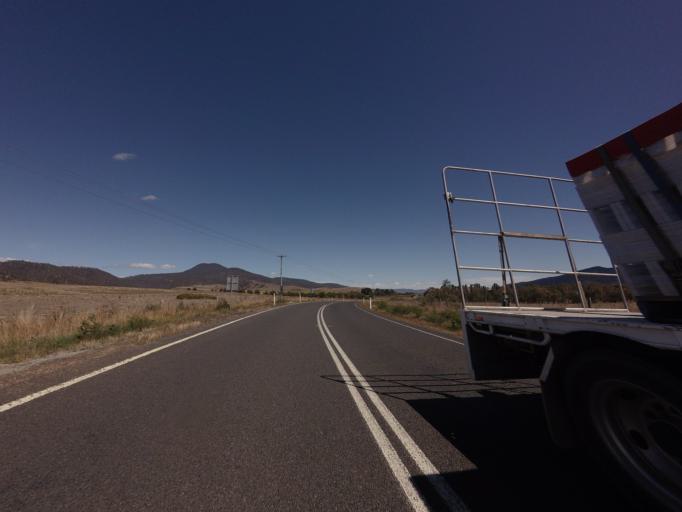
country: AU
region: Tasmania
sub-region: Break O'Day
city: St Helens
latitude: -41.7061
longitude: 147.8488
